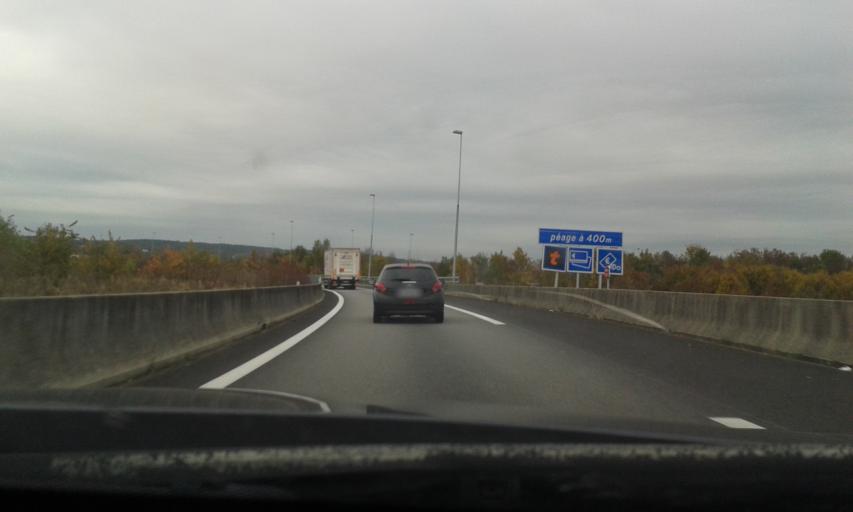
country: FR
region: Haute-Normandie
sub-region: Departement de l'Eure
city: Le Vaudreuil
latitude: 49.2443
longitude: 1.1859
